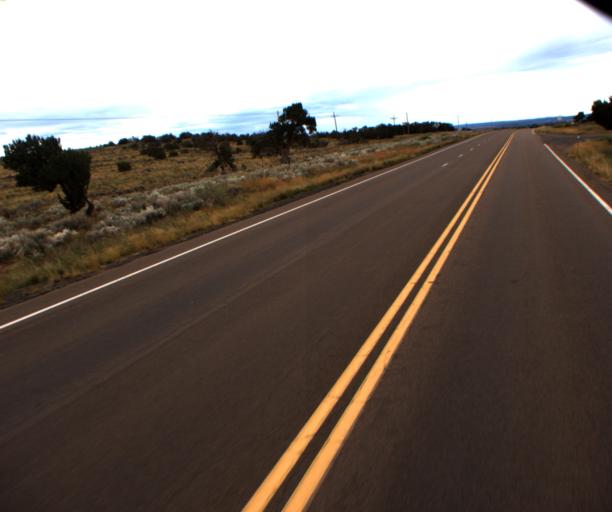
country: US
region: Arizona
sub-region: Navajo County
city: Snowflake
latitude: 34.5445
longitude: -110.0795
